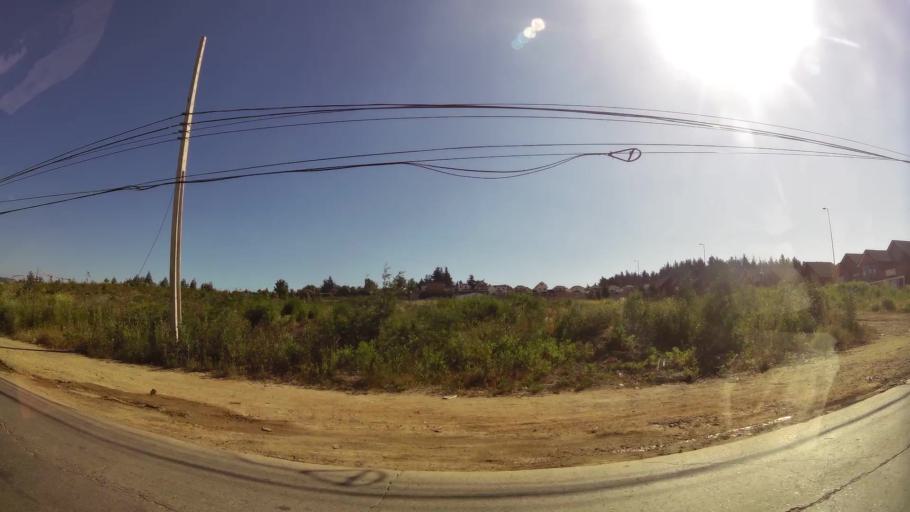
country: CL
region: Valparaiso
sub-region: Provincia de Valparaiso
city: Vina del Mar
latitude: -33.1291
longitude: -71.5680
